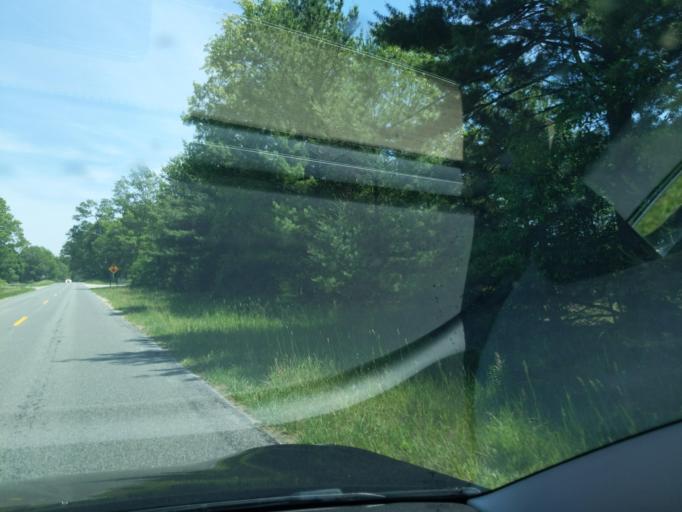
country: US
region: Michigan
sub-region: Muskegon County
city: Montague
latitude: 43.4154
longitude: -86.3794
